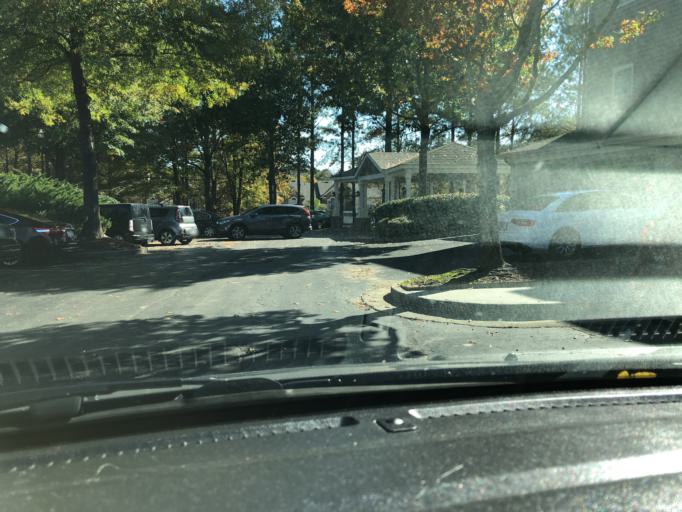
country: US
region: Georgia
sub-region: Fulton County
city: Johns Creek
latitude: 34.0158
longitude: -84.1810
